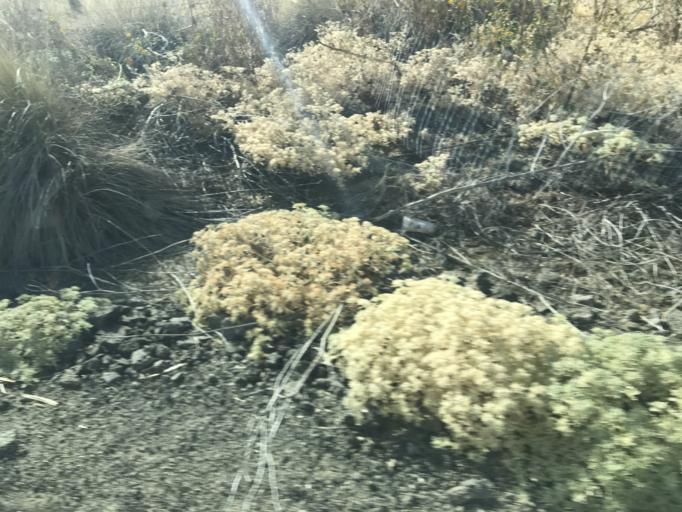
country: US
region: California
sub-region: Fresno County
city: Minkler
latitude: 36.8957
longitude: -119.4639
